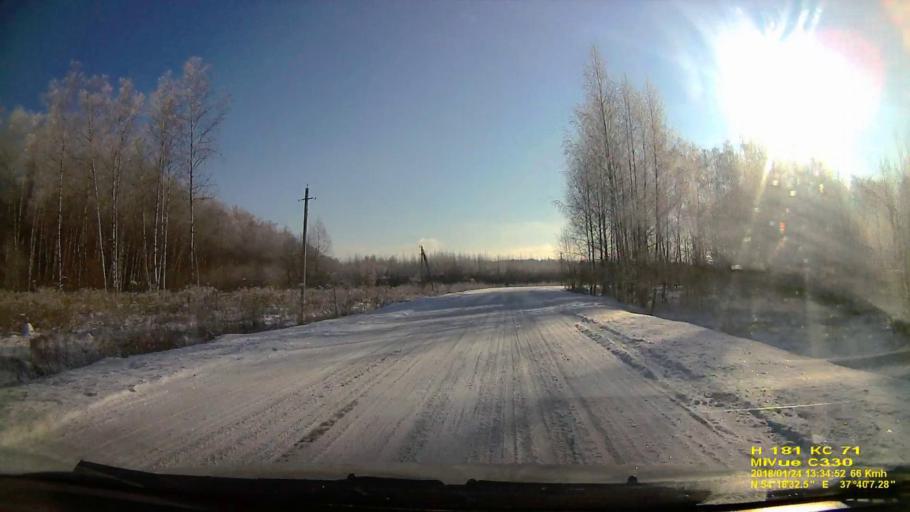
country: RU
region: Tula
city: Revyakino
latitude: 54.3090
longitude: 37.6687
